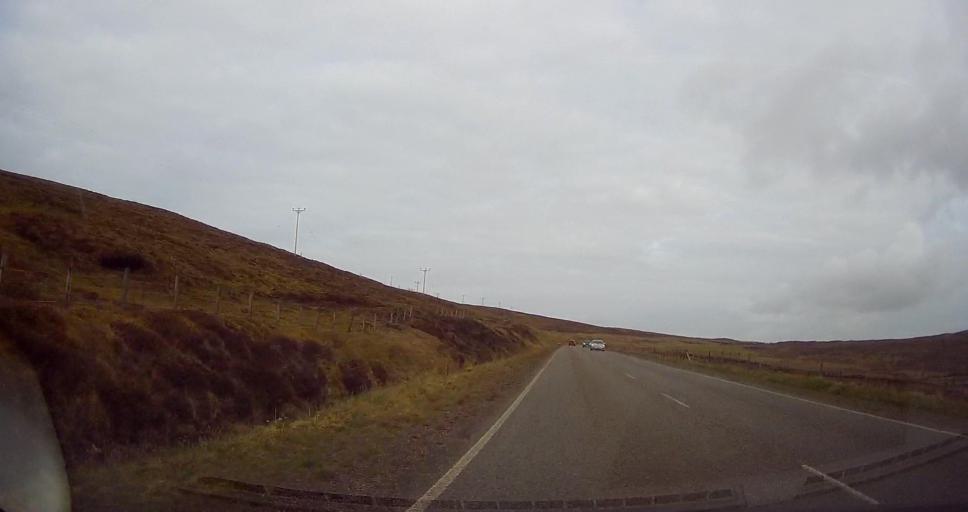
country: GB
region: Scotland
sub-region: Shetland Islands
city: Sandwick
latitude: 60.0821
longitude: -1.2310
